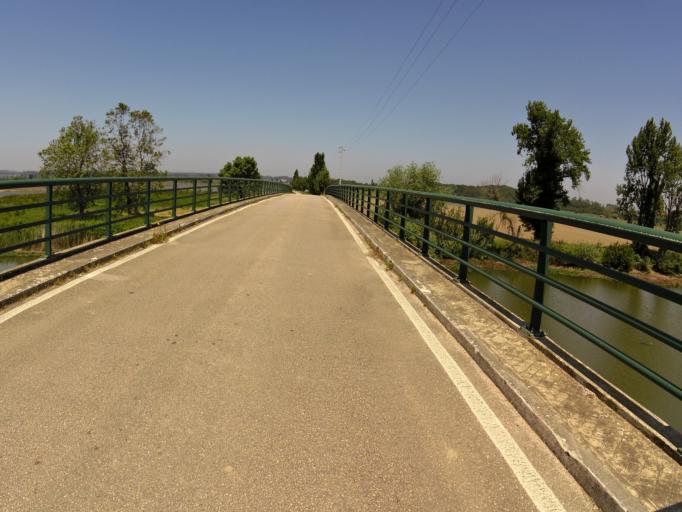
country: PT
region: Coimbra
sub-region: Montemor-O-Velho
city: Montemor-o-Velho
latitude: 40.1597
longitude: -8.7143
